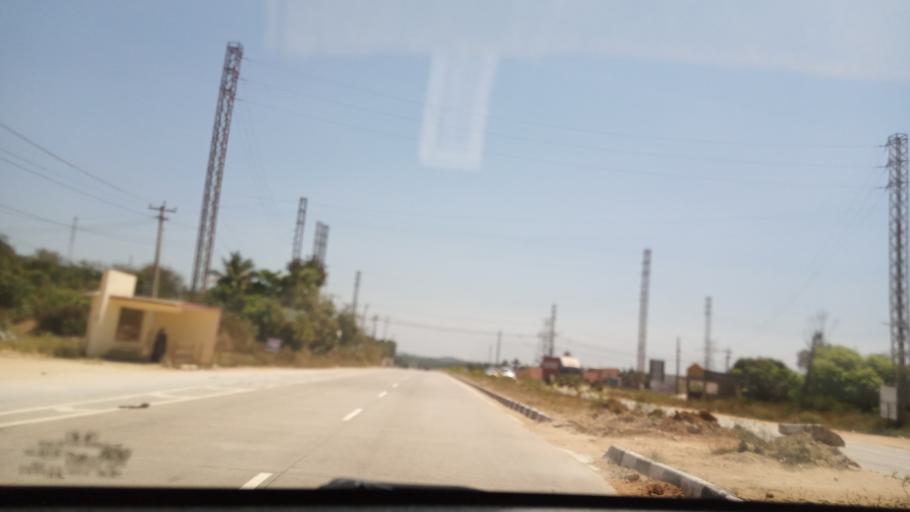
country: IN
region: Andhra Pradesh
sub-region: Chittoor
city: Chittoor
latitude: 13.1976
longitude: 78.9793
